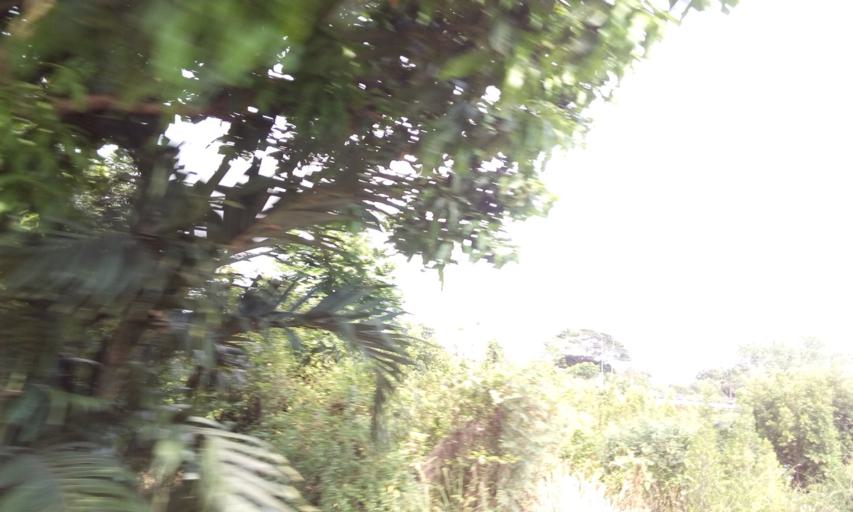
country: TH
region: Nakhon Nayok
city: Ongkharak
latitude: 14.0853
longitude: 100.9145
